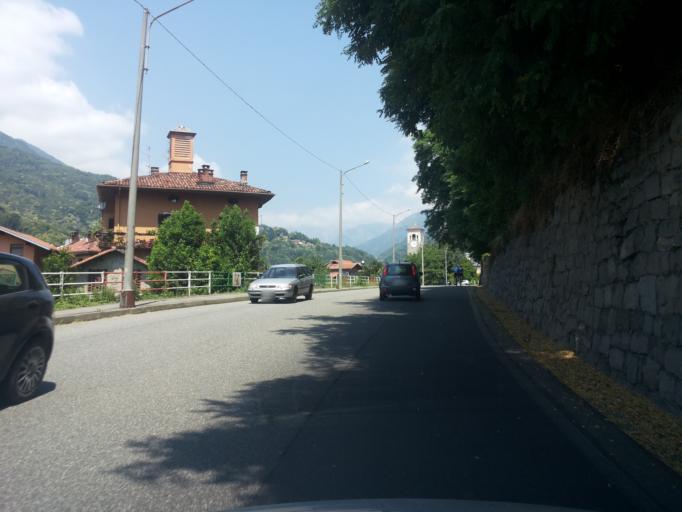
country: IT
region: Piedmont
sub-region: Provincia di Biella
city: Tavigliano
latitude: 45.6189
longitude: 8.0475
